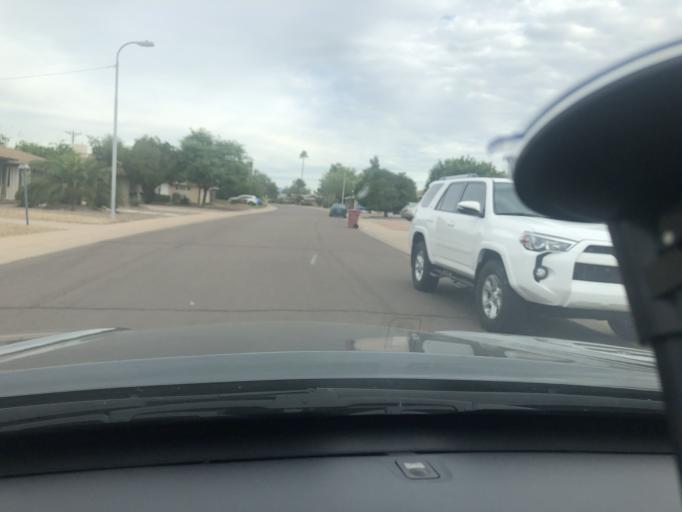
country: US
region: Arizona
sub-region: Maricopa County
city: Scottsdale
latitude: 33.4761
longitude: -111.9024
